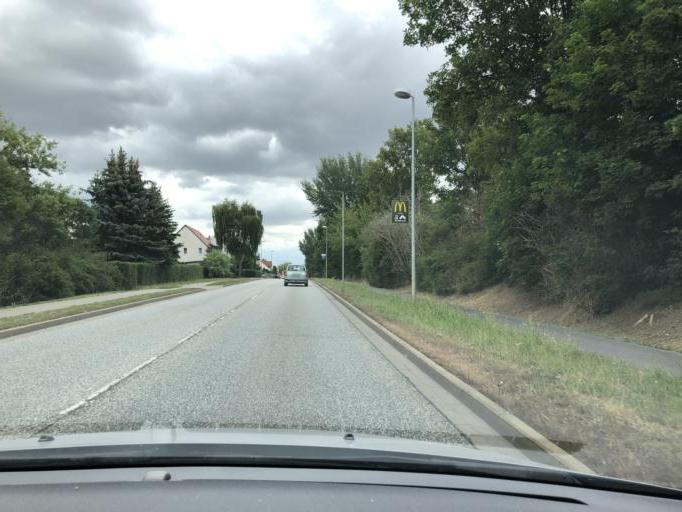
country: DE
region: Saxony-Anhalt
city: Volkstedt
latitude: 51.5202
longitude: 11.5599
